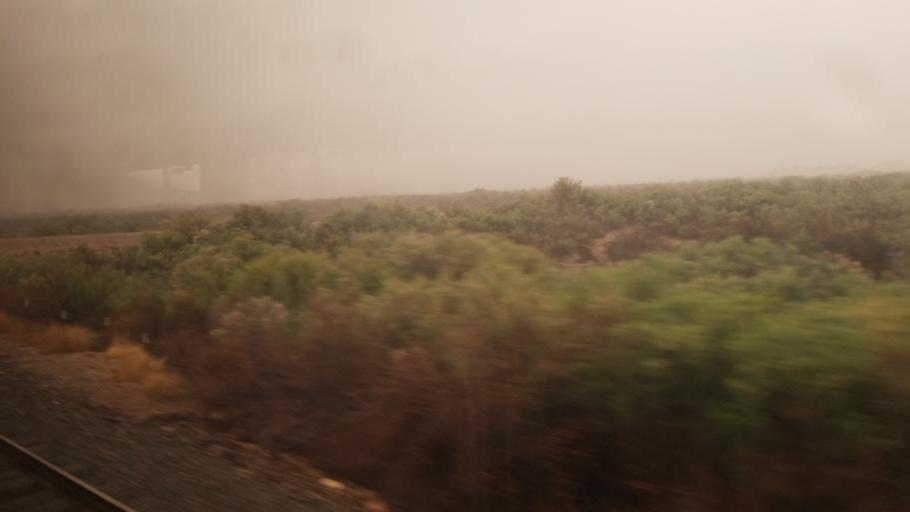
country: US
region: Arizona
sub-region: Navajo County
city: Joseph City
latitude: 34.9504
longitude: -110.3394
